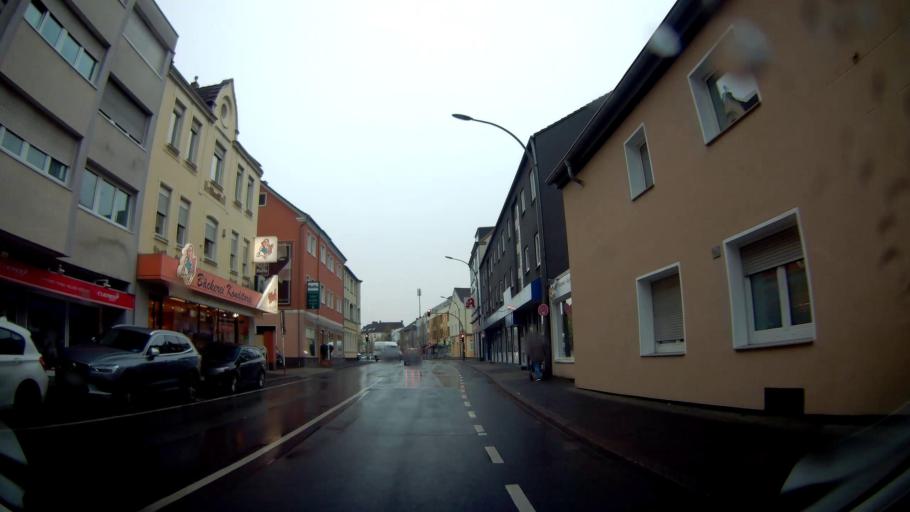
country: DE
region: North Rhine-Westphalia
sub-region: Regierungsbezirk Arnsberg
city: Dortmund
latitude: 51.5294
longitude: 7.4131
